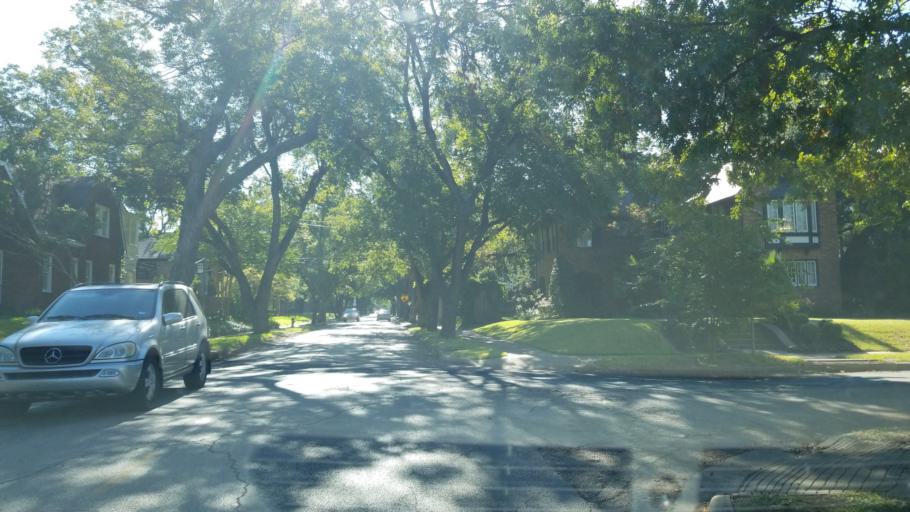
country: US
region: Texas
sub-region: Dallas County
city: Highland Park
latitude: 32.8111
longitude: -96.7613
